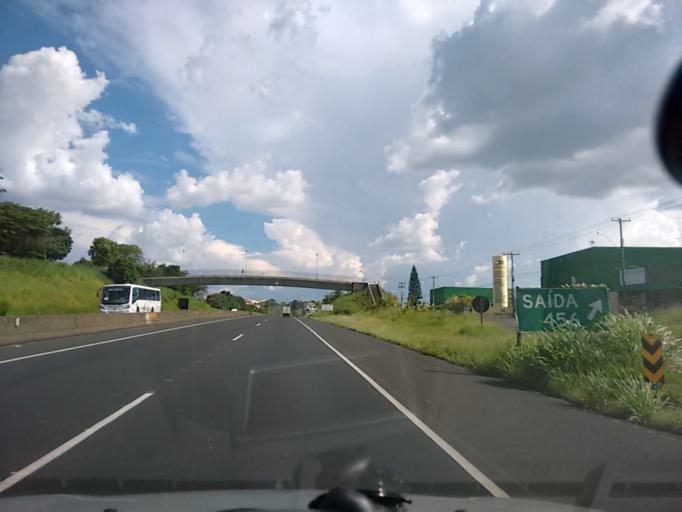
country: BR
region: Sao Paulo
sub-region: Marilia
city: Marilia
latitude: -22.1941
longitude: -49.9661
